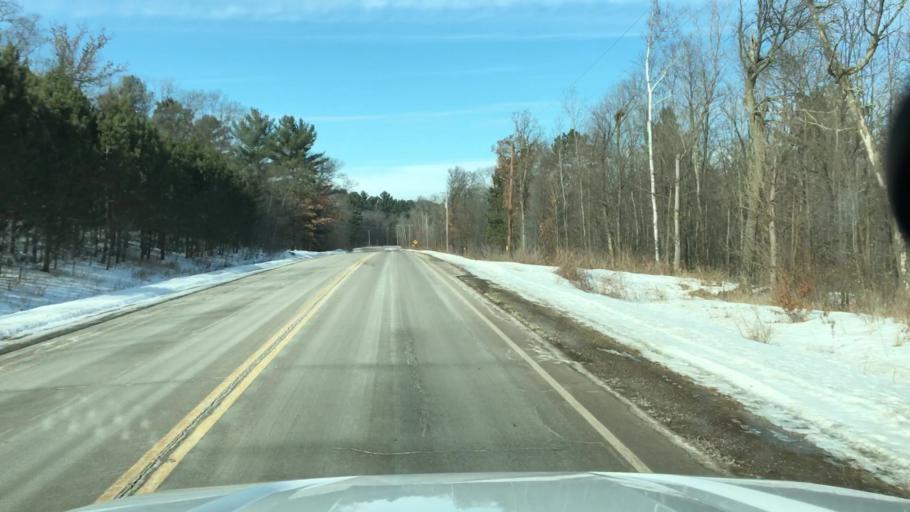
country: US
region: Wisconsin
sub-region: Polk County
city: Saint Croix Falls
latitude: 45.4632
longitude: -92.6821
